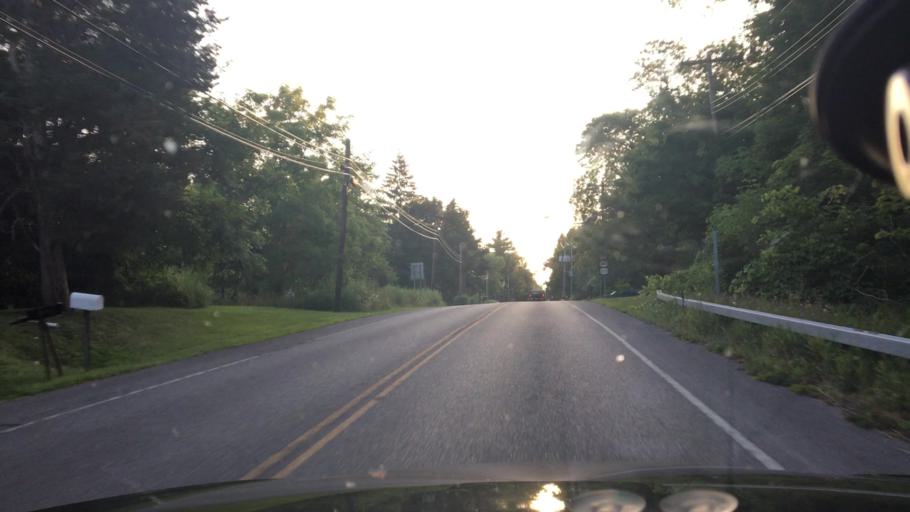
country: US
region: New York
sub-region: Erie County
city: Orchard Park
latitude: 42.7890
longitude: -78.7436
